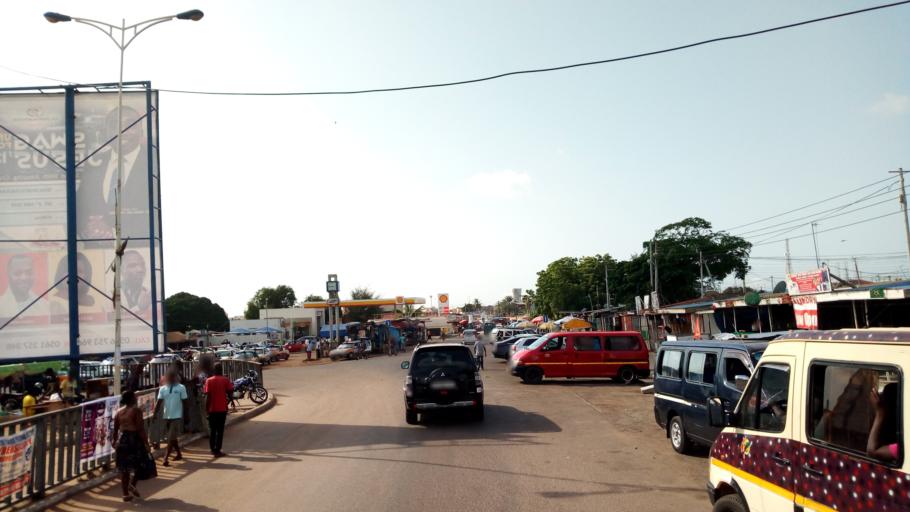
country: GH
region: Greater Accra
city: Tema
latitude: 5.6469
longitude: -0.0023
